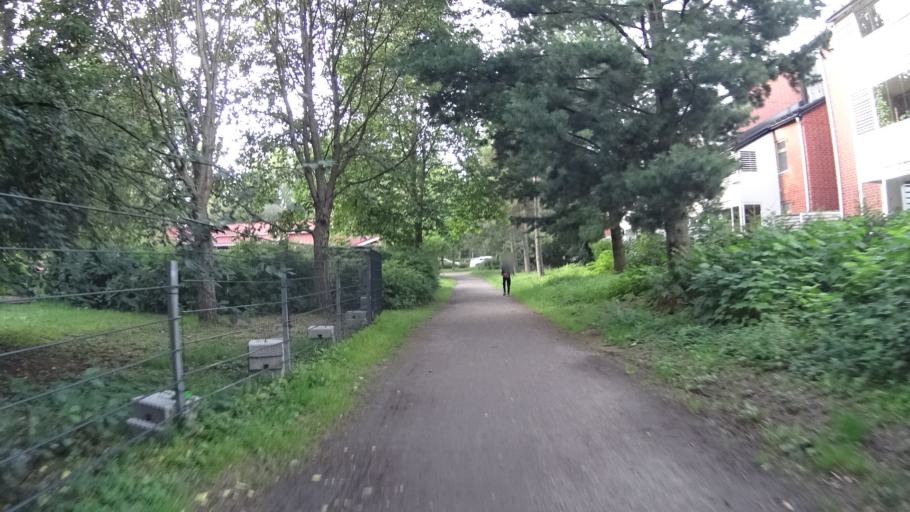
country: FI
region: Uusimaa
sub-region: Helsinki
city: Teekkarikylae
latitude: 60.2318
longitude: 24.8784
